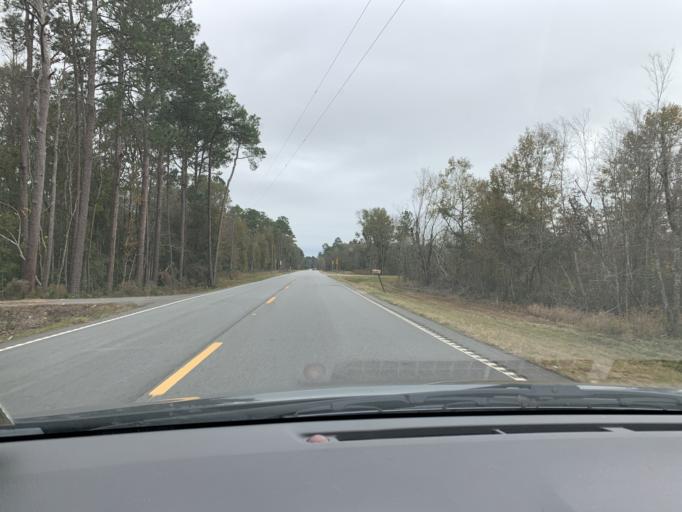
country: US
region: Georgia
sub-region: Thomas County
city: Meigs
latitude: 31.0167
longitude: -83.9599
